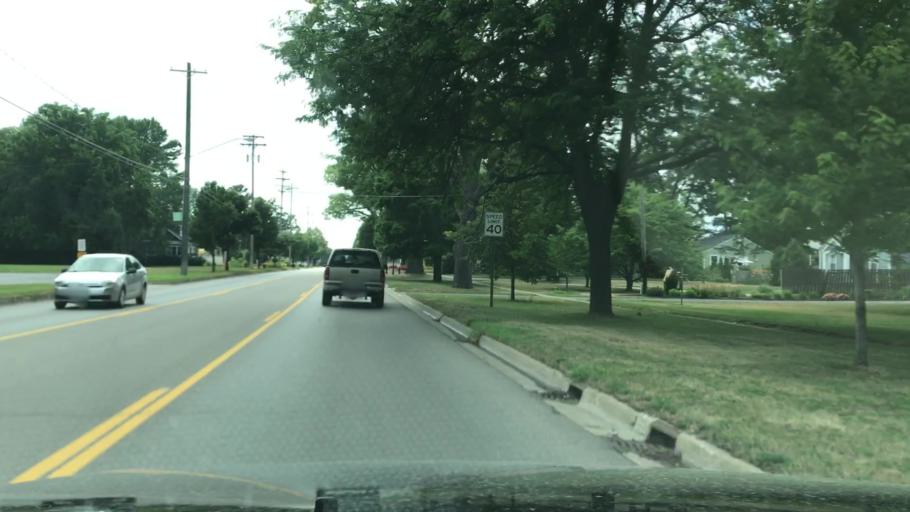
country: US
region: Michigan
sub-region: Ottawa County
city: Spring Lake
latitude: 43.0768
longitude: -86.1791
